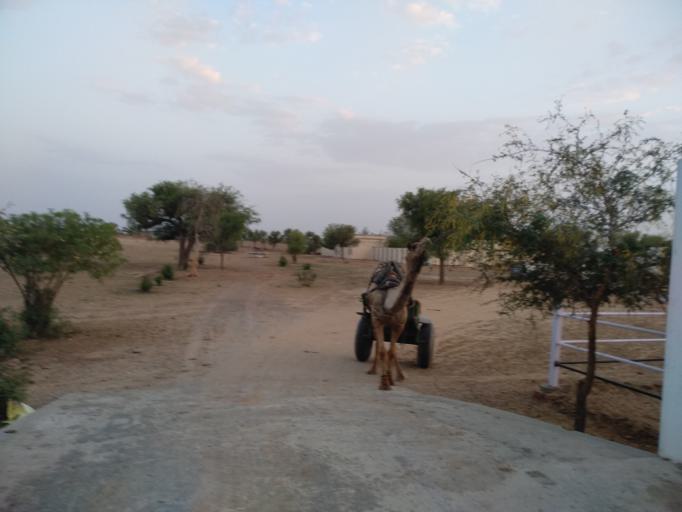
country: IN
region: Rajasthan
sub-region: Sikar
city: Fatehpur
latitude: 28.0413
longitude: 75.1514
